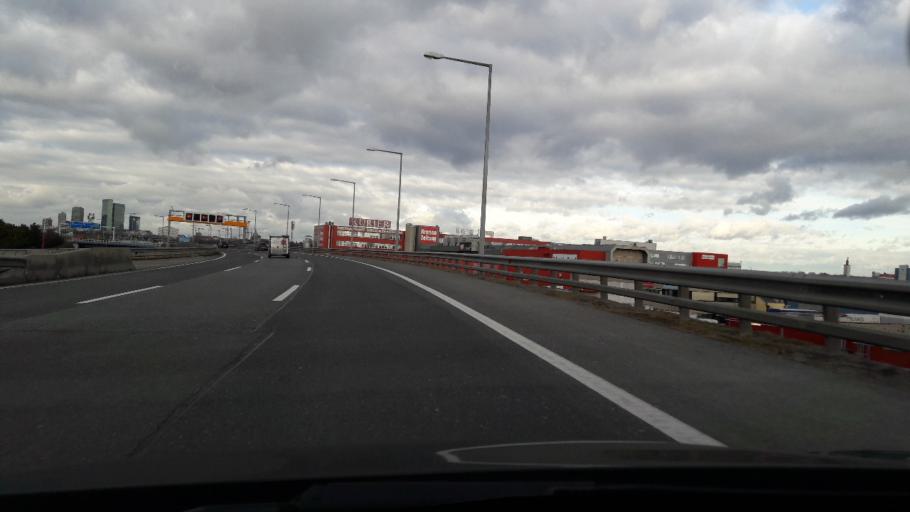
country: AT
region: Lower Austria
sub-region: Politischer Bezirk Modling
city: Vosendorf
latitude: 48.1419
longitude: 16.3353
